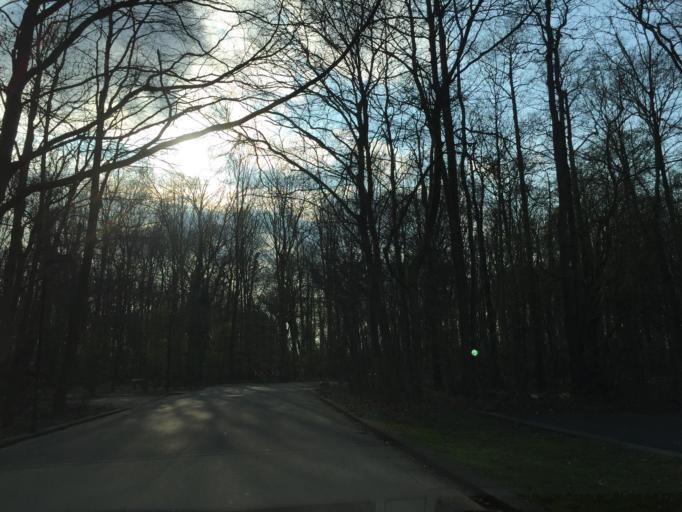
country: DK
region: South Denmark
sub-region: Odense Kommune
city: Neder Holluf
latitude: 55.3659
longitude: 10.4264
